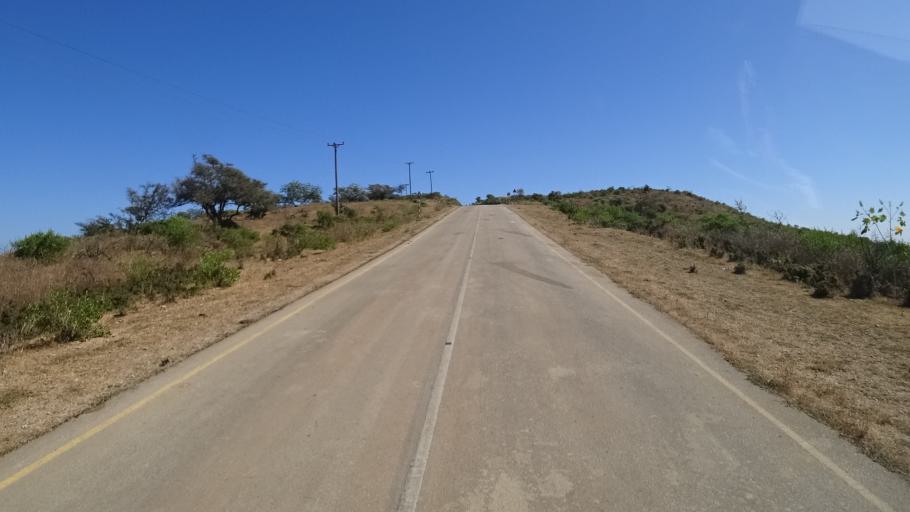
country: YE
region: Al Mahrah
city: Hawf
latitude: 16.7442
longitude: 53.3599
